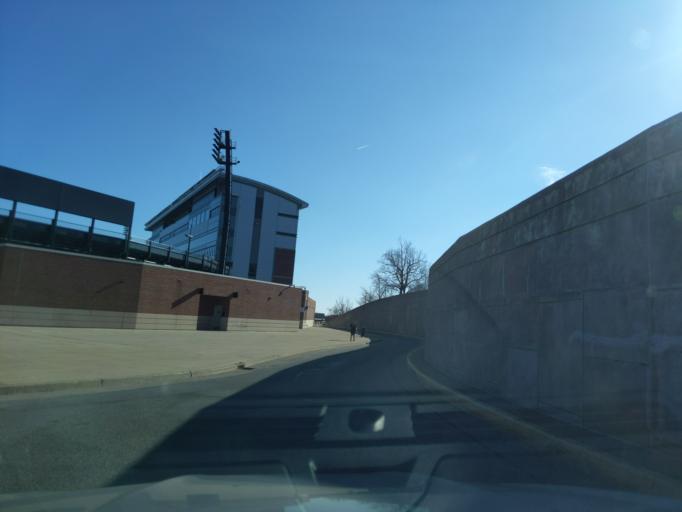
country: US
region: Indiana
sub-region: Tippecanoe County
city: West Lafayette
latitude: 40.4358
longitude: -86.9195
